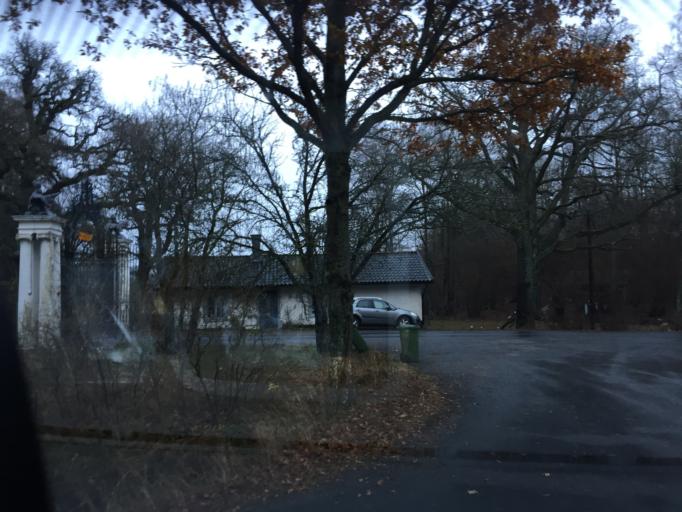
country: SE
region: Stockholm
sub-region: Nynashamns Kommun
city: Osmo
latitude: 59.0509
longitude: 18.0155
